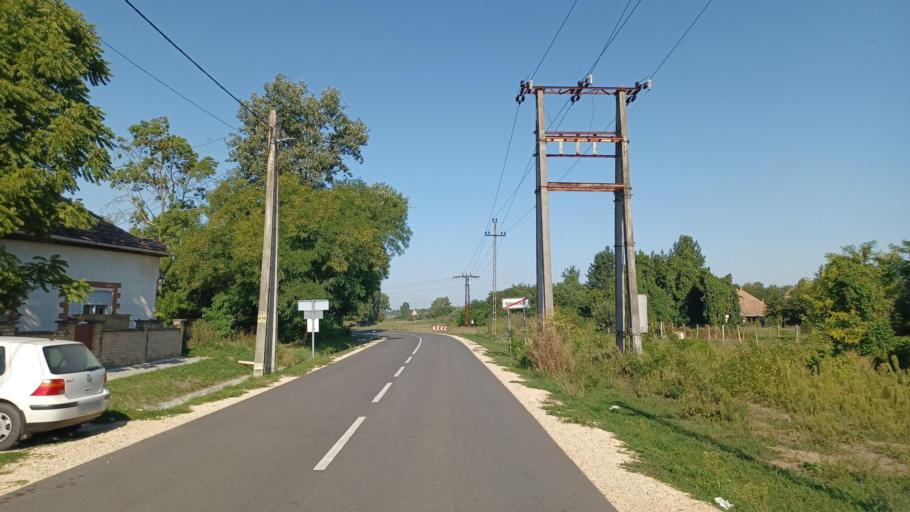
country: HU
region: Tolna
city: Nemetker
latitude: 46.7308
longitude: 18.7471
